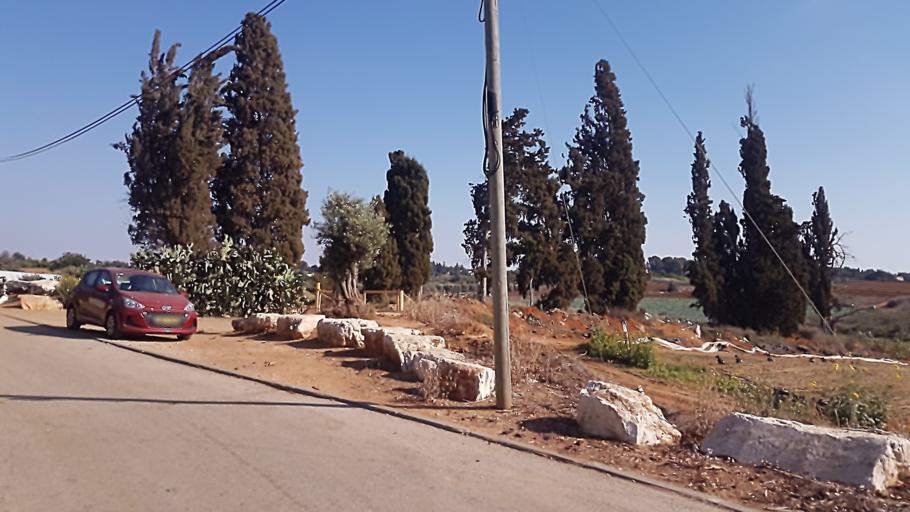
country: IL
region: Central District
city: Kfar Saba
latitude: 32.2030
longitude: 34.9056
